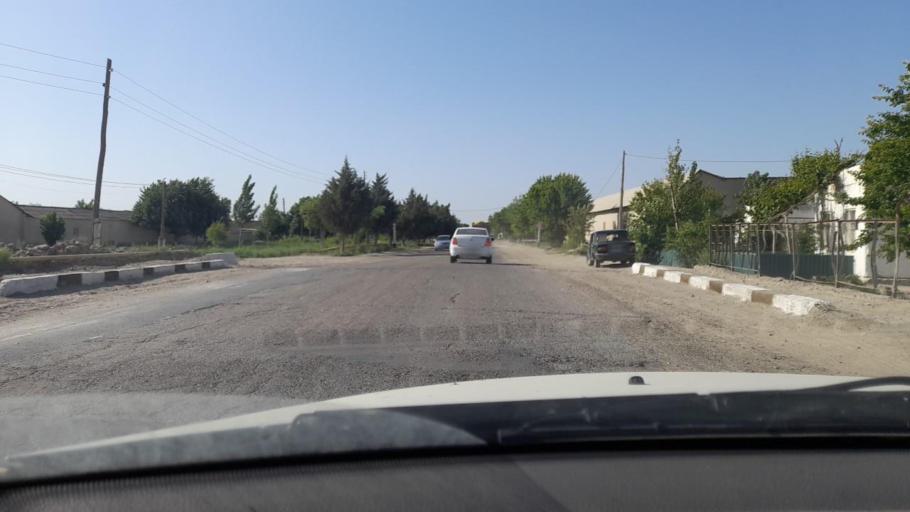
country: UZ
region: Bukhara
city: Romiton
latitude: 40.0631
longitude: 64.3271
